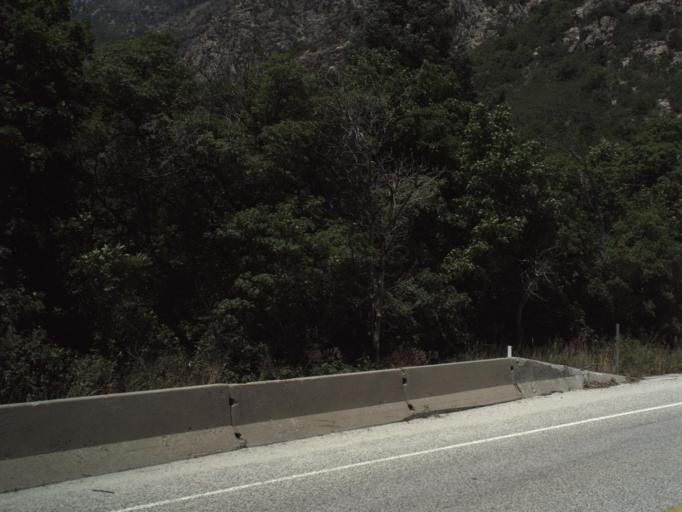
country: US
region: Utah
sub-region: Weber County
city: Ogden
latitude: 41.2434
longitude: -111.8959
